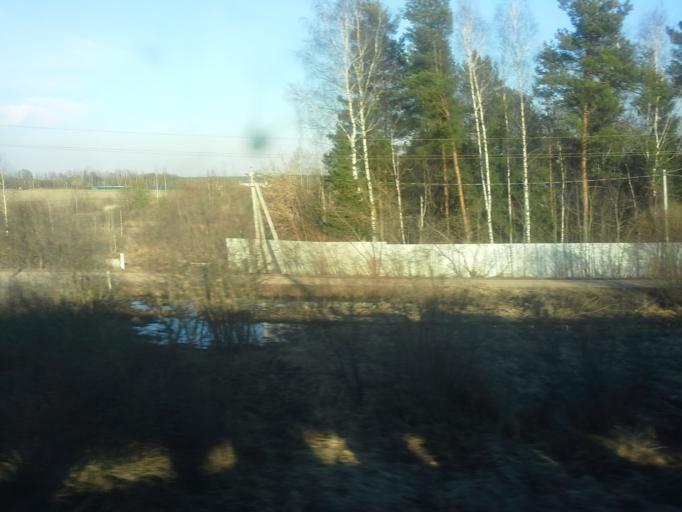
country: RU
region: Moskovskaya
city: Nekrasovskiy
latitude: 56.0809
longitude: 37.4995
